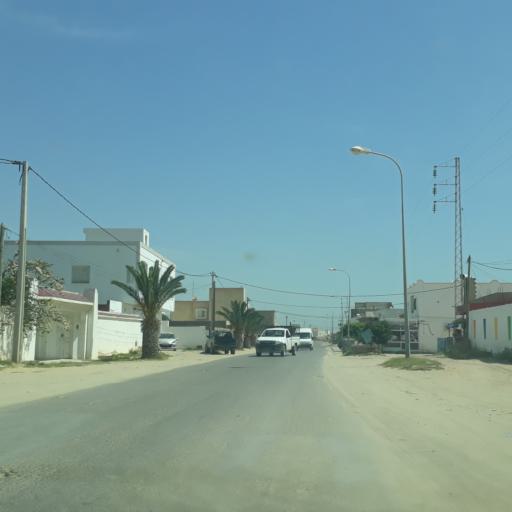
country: TN
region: Safaqis
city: Al Qarmadah
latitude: 34.8199
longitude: 10.7779
